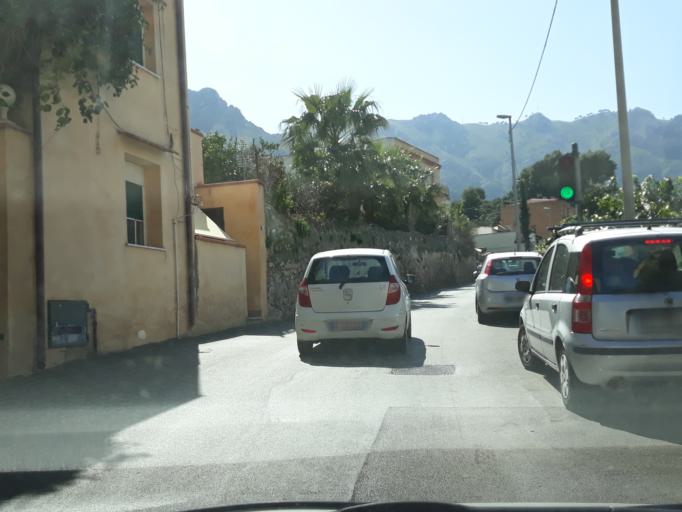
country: IT
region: Sicily
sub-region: Palermo
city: Ciaculli
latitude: 38.0837
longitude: 13.3769
